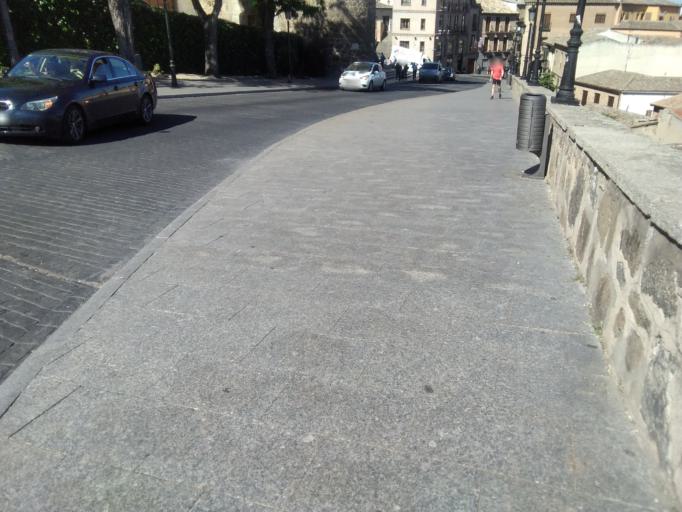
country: ES
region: Castille-La Mancha
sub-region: Province of Toledo
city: Toledo
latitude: 39.8613
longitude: -4.0234
